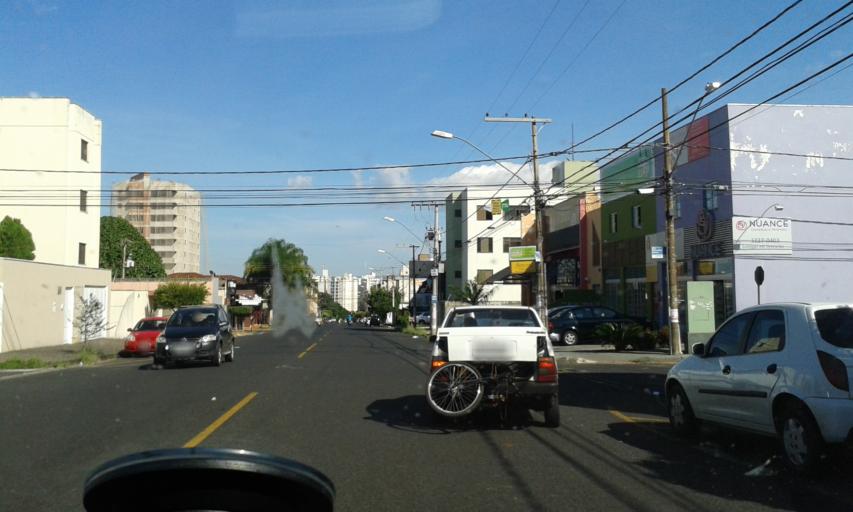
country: BR
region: Minas Gerais
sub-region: Uberlandia
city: Uberlandia
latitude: -18.9226
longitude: -48.2472
